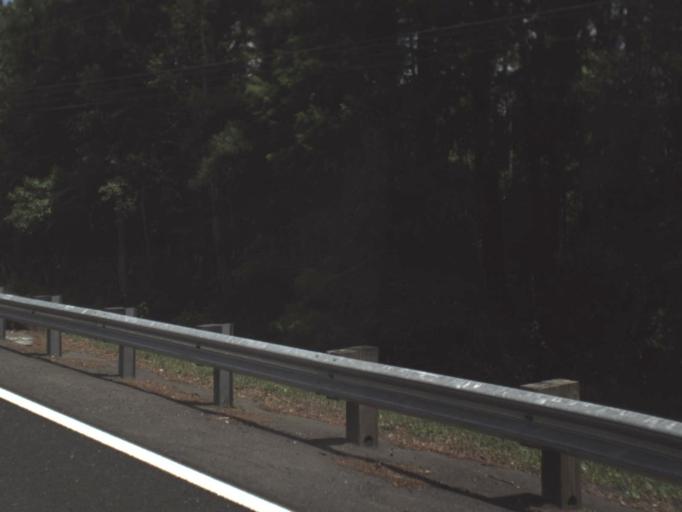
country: US
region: Florida
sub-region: Saint Johns County
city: Fruit Cove
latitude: 30.1517
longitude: -81.5257
